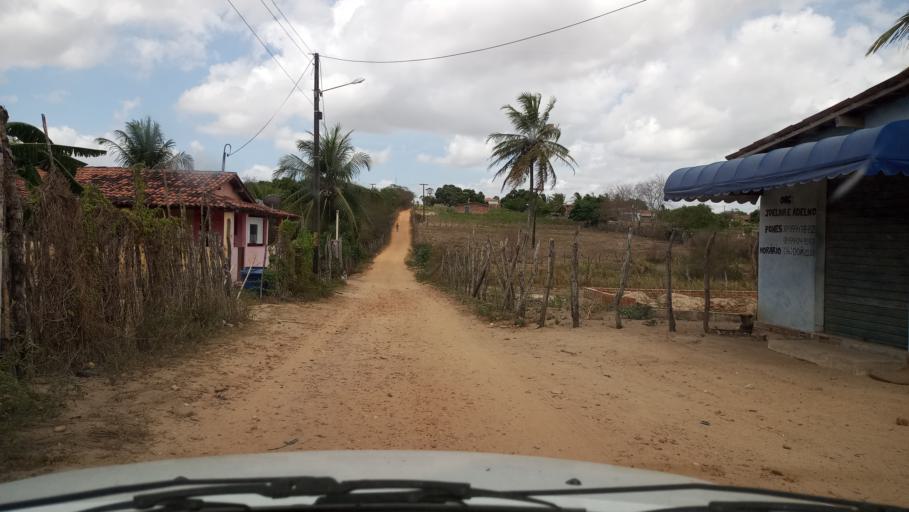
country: BR
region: Rio Grande do Norte
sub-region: Goianinha
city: Goianinha
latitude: -6.3011
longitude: -35.2752
